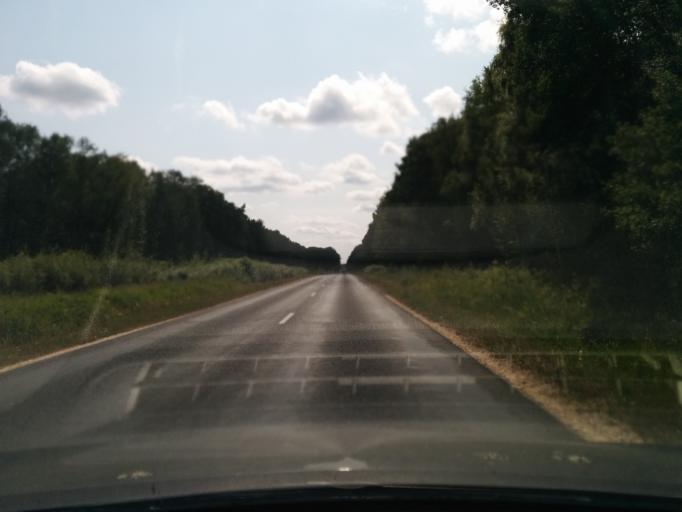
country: FR
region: Centre
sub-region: Departement du Cher
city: Neuvy-sur-Barangeon
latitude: 47.2933
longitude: 2.2105
